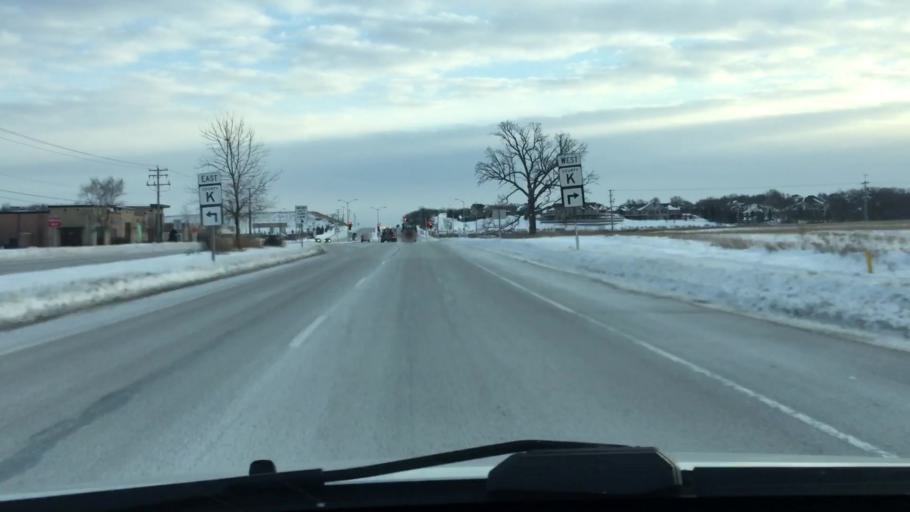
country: US
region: Wisconsin
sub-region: Waukesha County
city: Sussex
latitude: 43.1144
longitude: -88.2448
